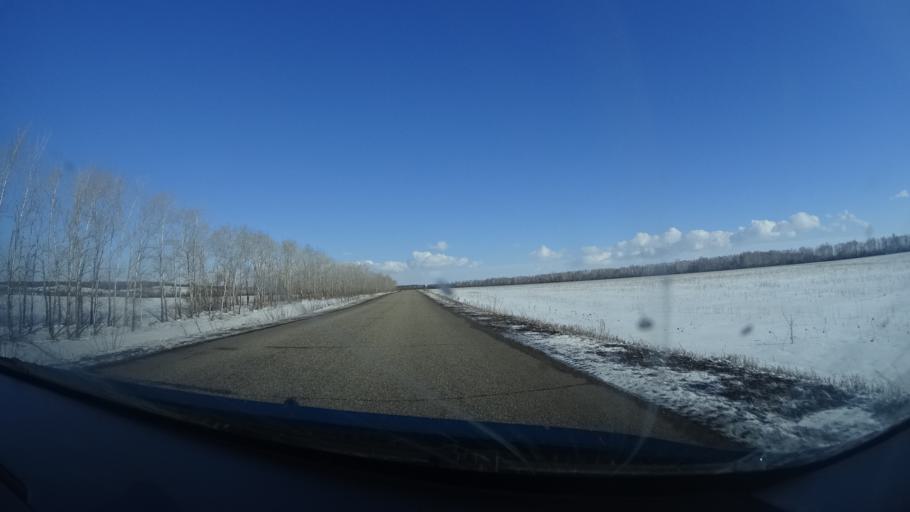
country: RU
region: Bashkortostan
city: Chishmy
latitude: 54.5906
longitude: 55.3063
